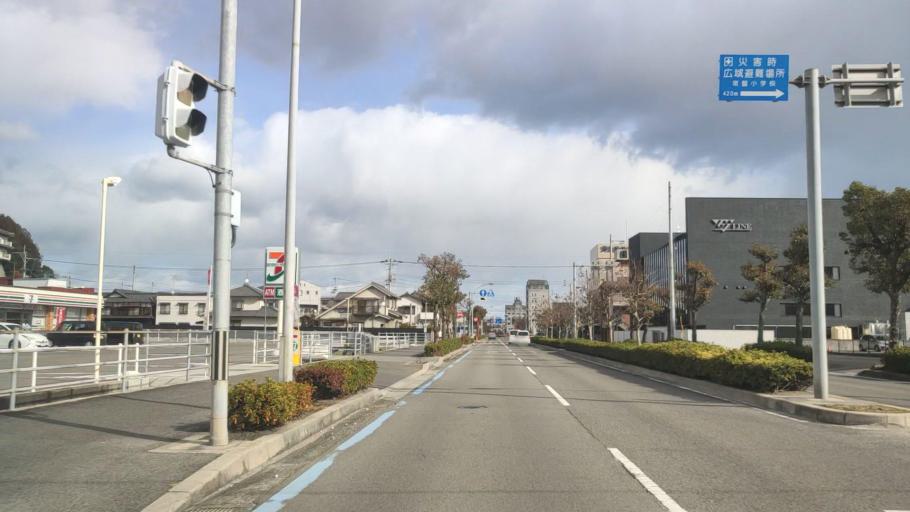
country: JP
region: Ehime
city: Hojo
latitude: 34.0627
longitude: 132.9867
